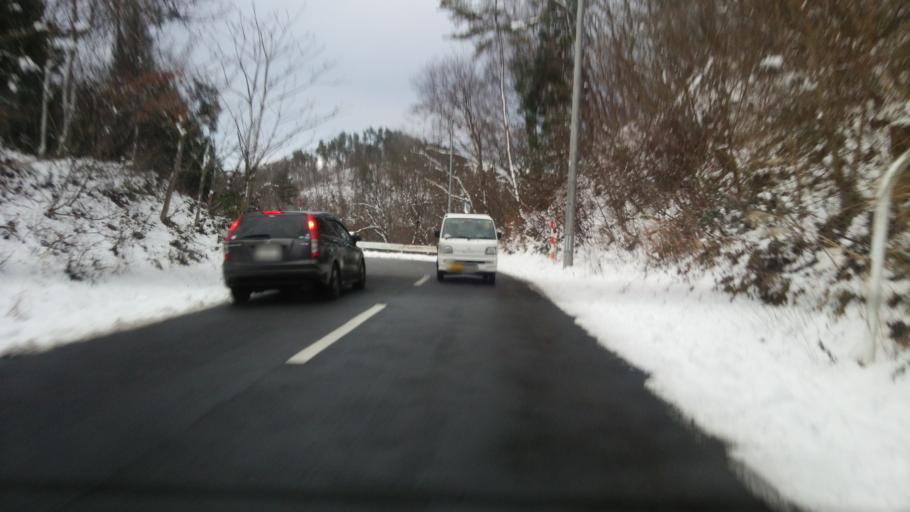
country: JP
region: Fukushima
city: Kitakata
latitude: 37.5693
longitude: 139.9481
